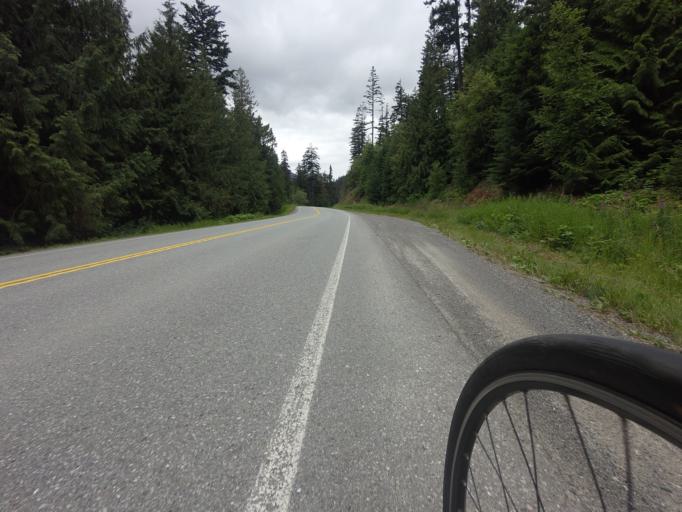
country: CA
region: British Columbia
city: Lillooet
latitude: 50.5185
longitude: -122.1680
